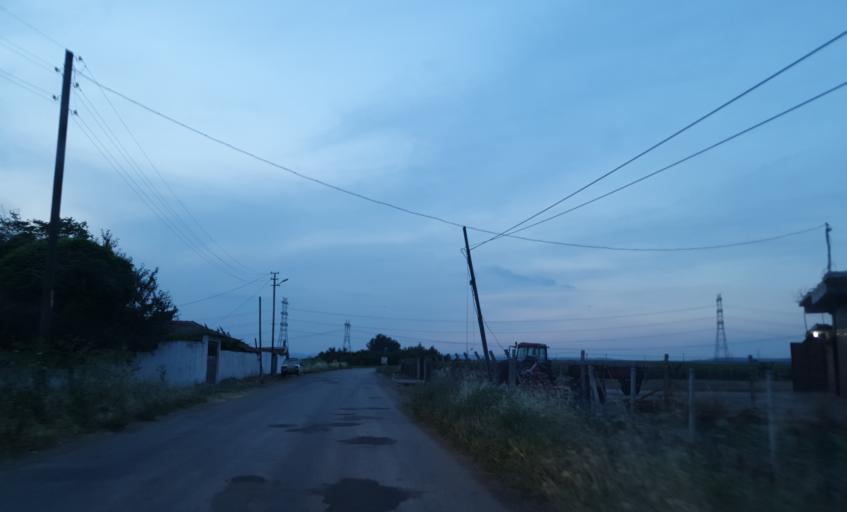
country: TR
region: Kirklareli
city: Vize
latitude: 41.4902
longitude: 27.7521
